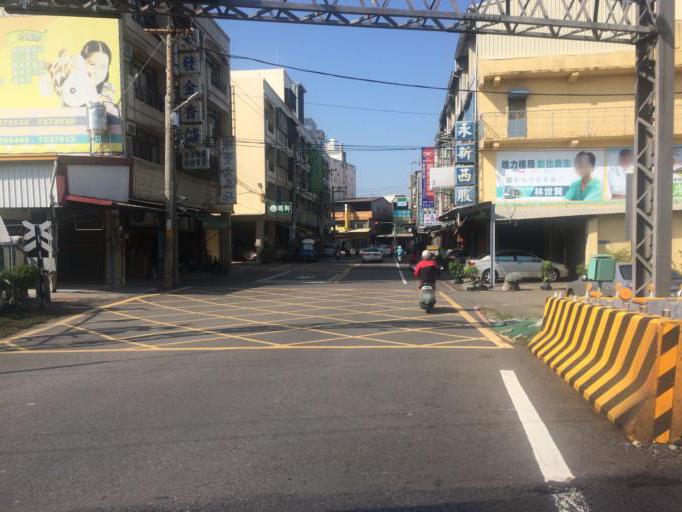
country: TW
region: Taiwan
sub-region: Changhua
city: Chang-hua
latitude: 24.0895
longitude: 120.5493
